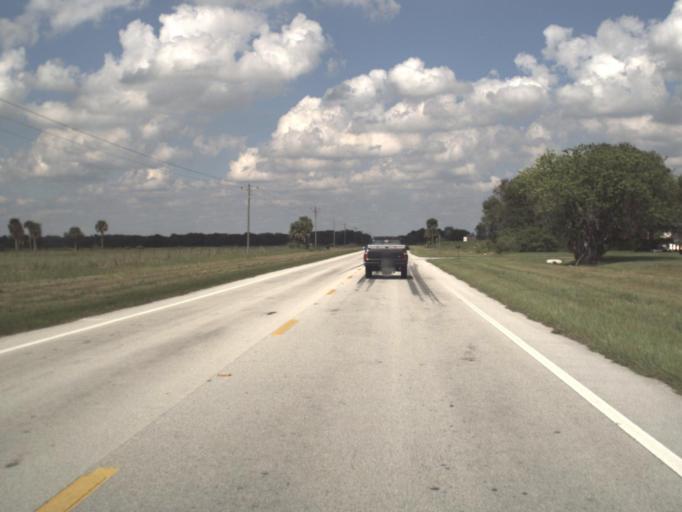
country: US
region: Florida
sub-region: Okeechobee County
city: Okeechobee
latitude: 27.3043
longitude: -80.8990
